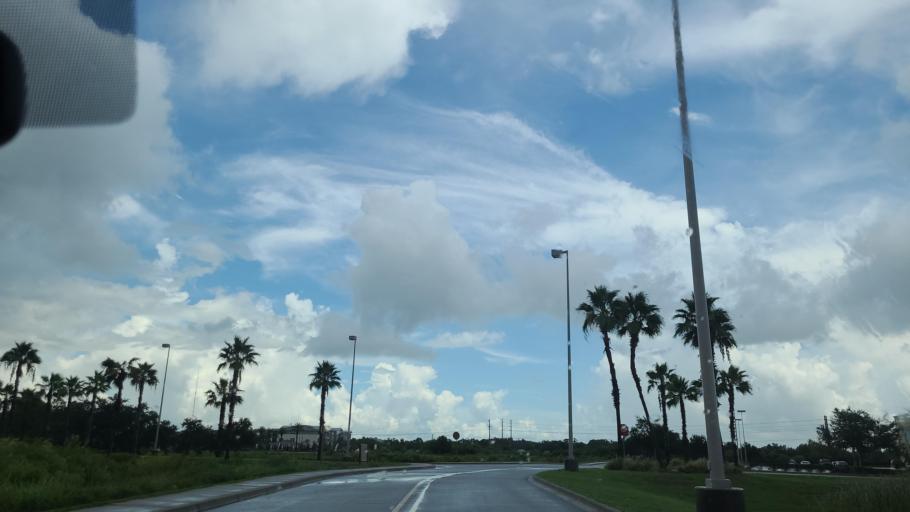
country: US
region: Florida
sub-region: Brevard County
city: West Melbourne
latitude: 28.0399
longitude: -80.6631
